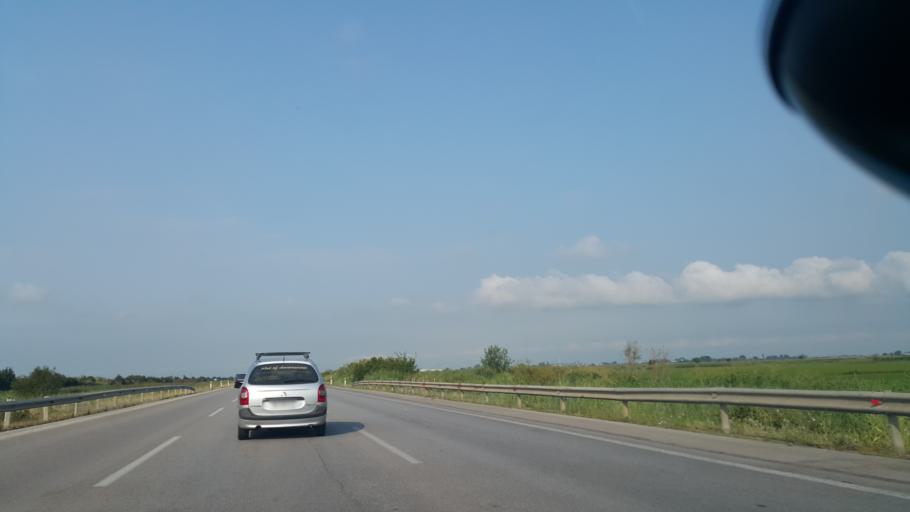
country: GR
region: Central Macedonia
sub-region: Nomos Thessalonikis
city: Sindos
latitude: 40.6387
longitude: 22.7908
